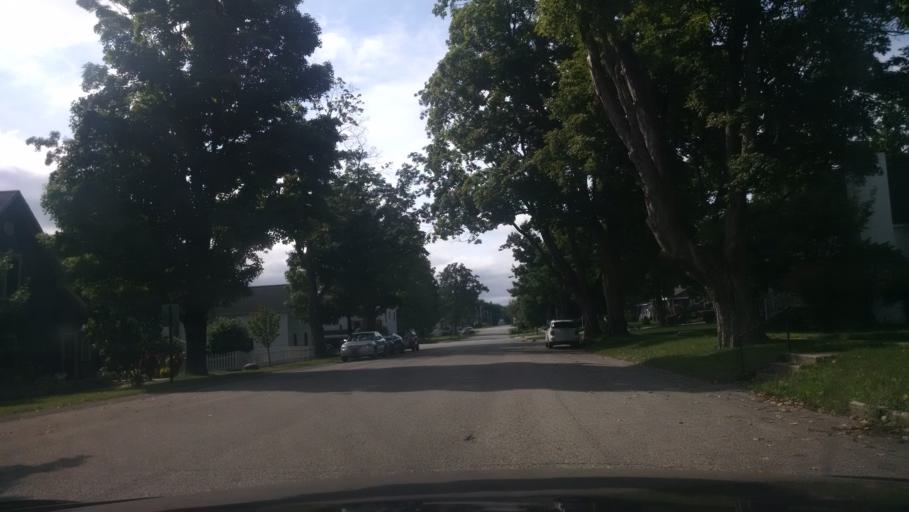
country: US
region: Michigan
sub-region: Leelanau County
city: Leland
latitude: 44.9764
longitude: -85.6525
